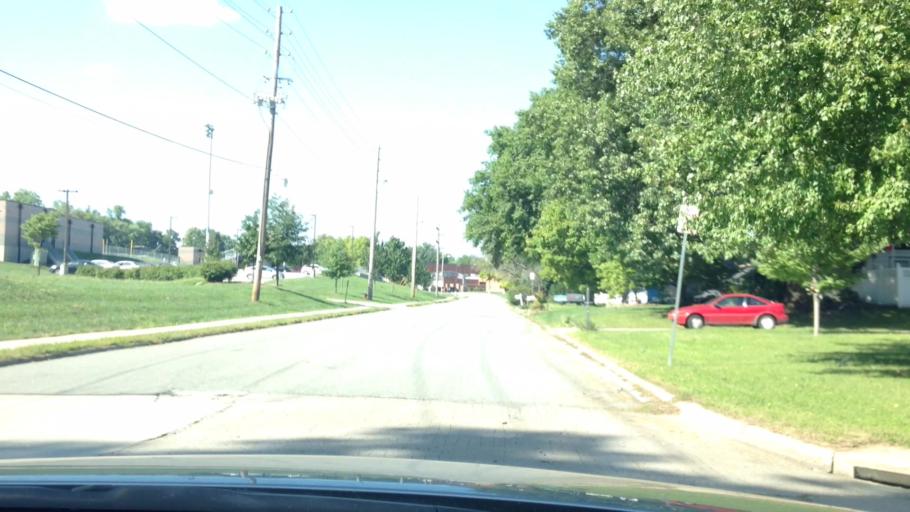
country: US
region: Kansas
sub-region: Leavenworth County
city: Leavenworth
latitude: 39.2932
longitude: -94.9301
